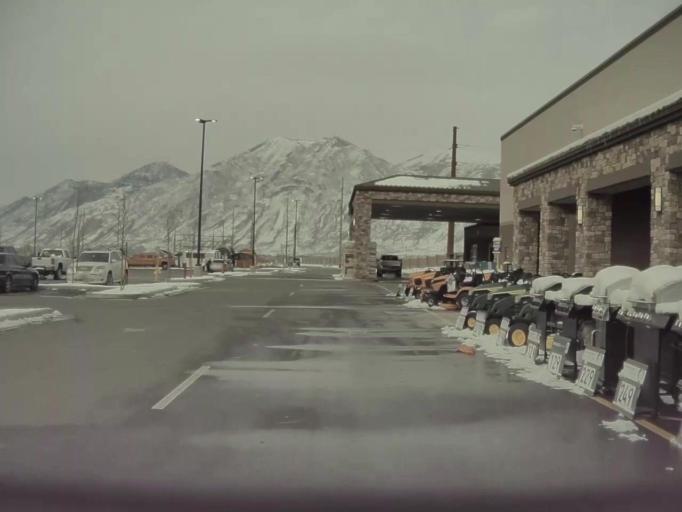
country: US
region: Utah
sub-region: Utah County
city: Spanish Fork
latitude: 40.1269
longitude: -111.6364
